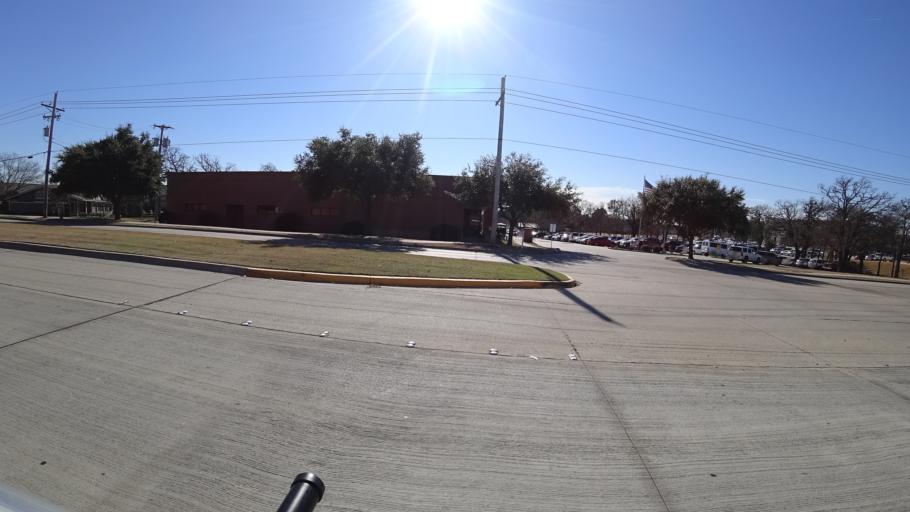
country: US
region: Texas
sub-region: Denton County
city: Lewisville
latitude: 33.0277
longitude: -97.0151
